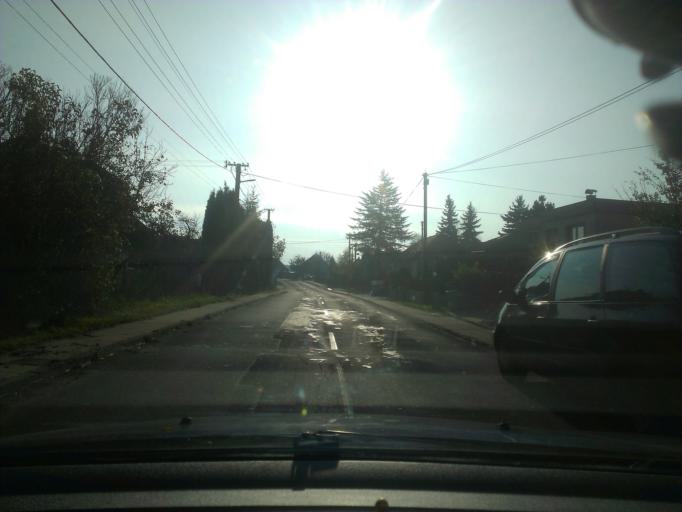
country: SK
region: Trnavsky
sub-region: Okres Trnava
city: Piestany
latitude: 48.5189
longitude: 17.9718
